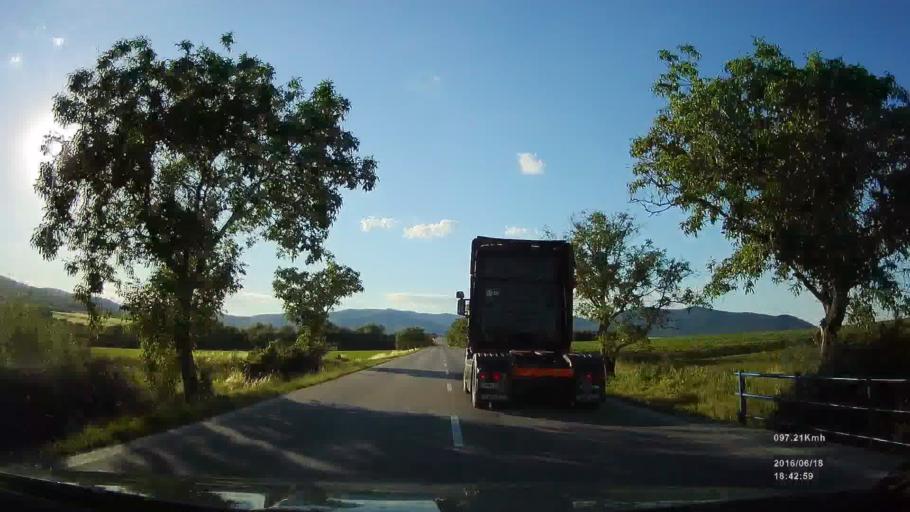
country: SK
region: Kosicky
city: Secovce
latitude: 48.7125
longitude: 21.6174
